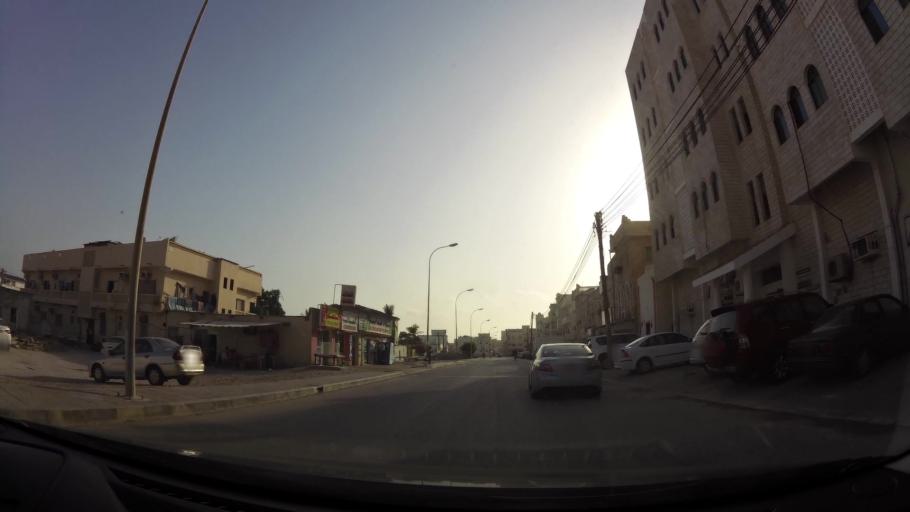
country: OM
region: Zufar
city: Salalah
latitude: 17.0106
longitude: 54.0887
